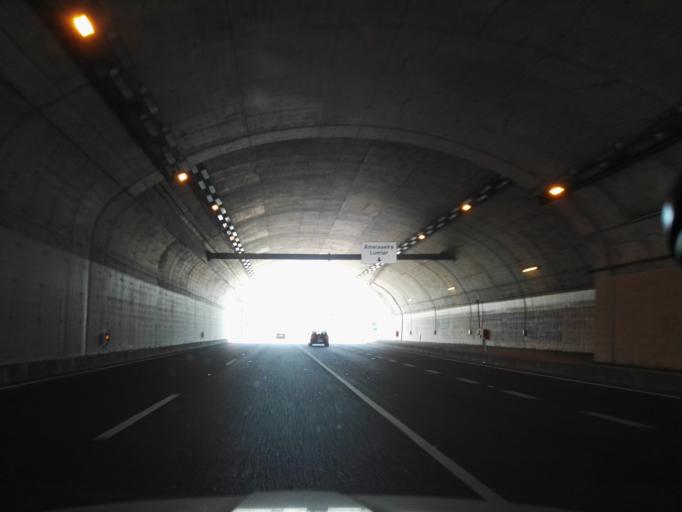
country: PT
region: Lisbon
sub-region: Odivelas
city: Olival do Basto
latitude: 38.7859
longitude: -9.1540
